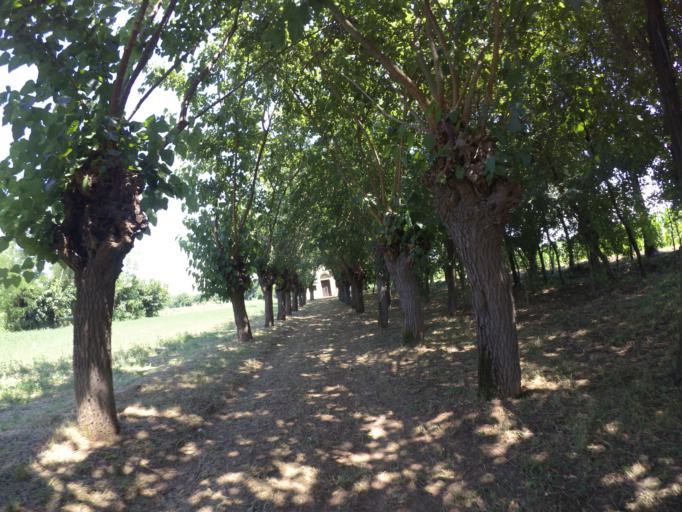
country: IT
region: Friuli Venezia Giulia
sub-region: Provincia di Udine
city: Mortegliano
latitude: 45.9323
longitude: 13.1813
